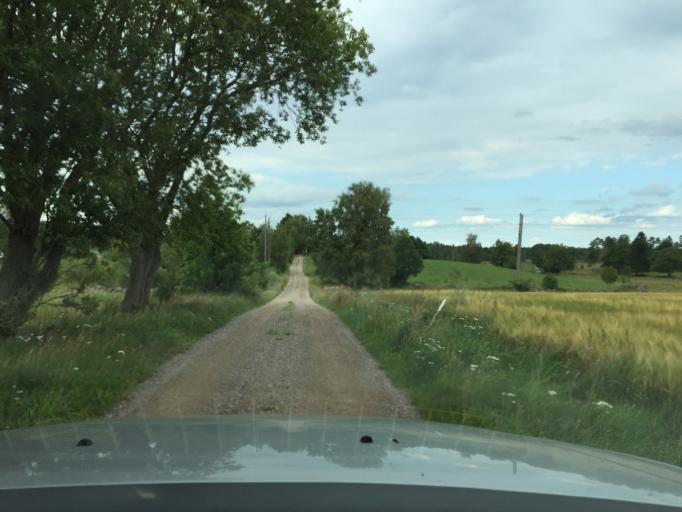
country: SE
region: Skane
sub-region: Hassleholms Kommun
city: Sosdala
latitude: 56.0498
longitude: 13.6897
